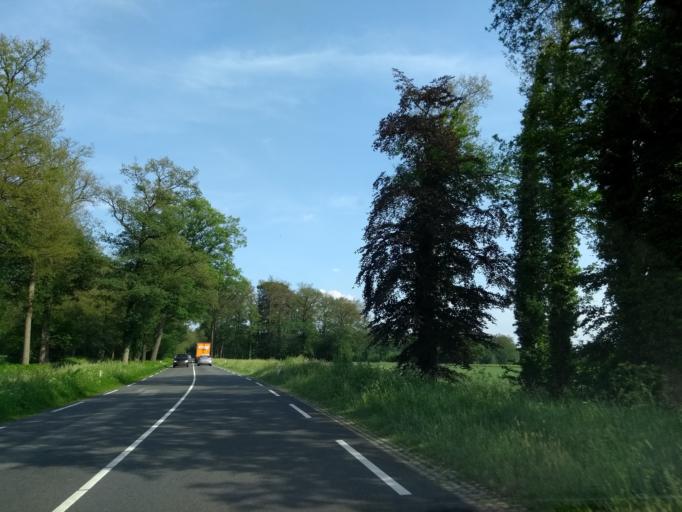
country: DE
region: Lower Saxony
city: Lage
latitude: 52.3980
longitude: 6.9572
